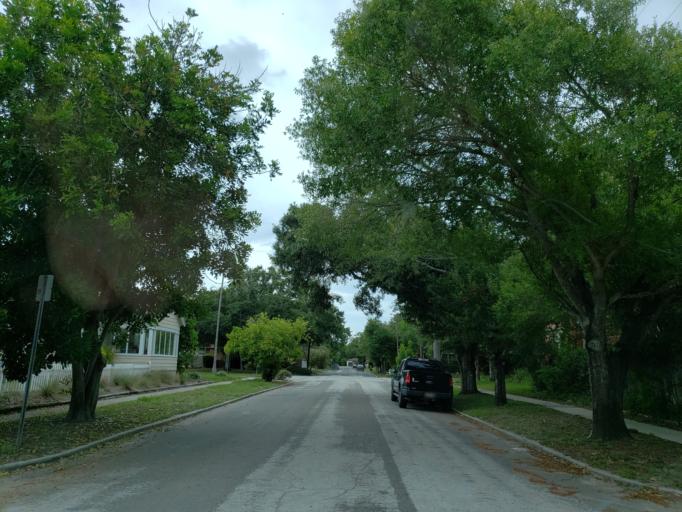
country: US
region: Florida
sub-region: Pinellas County
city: Saint Petersburg
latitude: 27.7786
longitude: -82.6769
